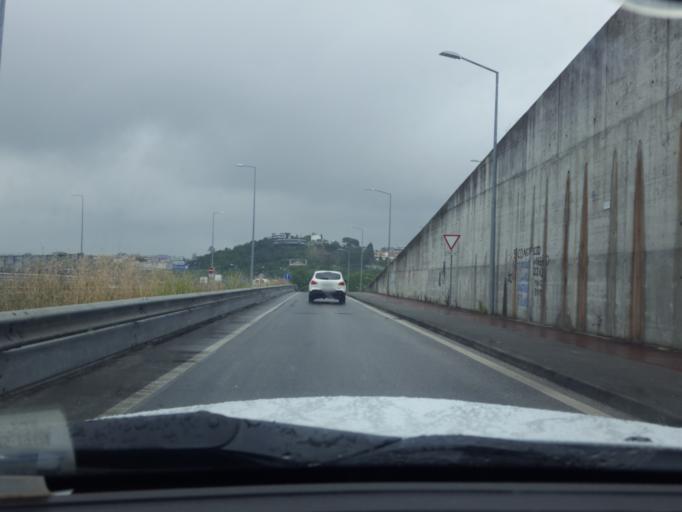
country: PT
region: Leiria
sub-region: Leiria
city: Leiria
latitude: 39.7363
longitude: -8.8221
